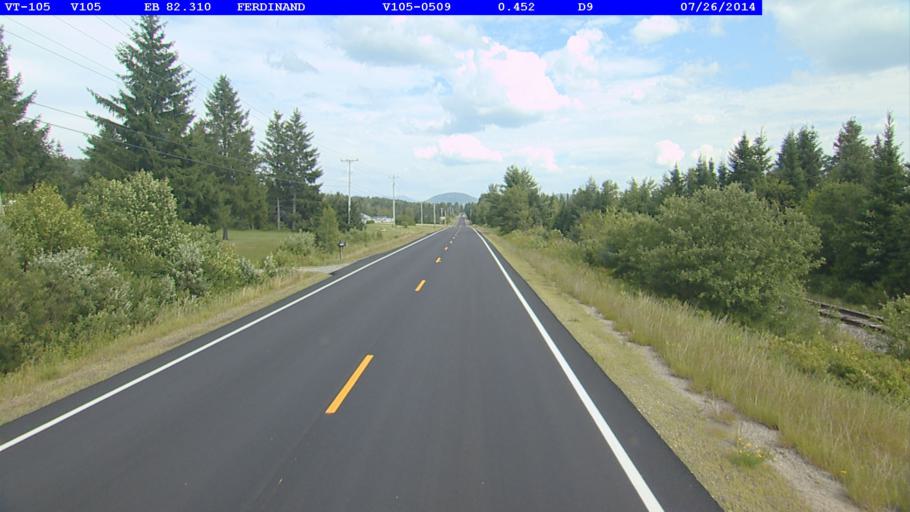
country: US
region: New Hampshire
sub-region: Coos County
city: Stratford
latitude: 44.7836
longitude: -71.7948
